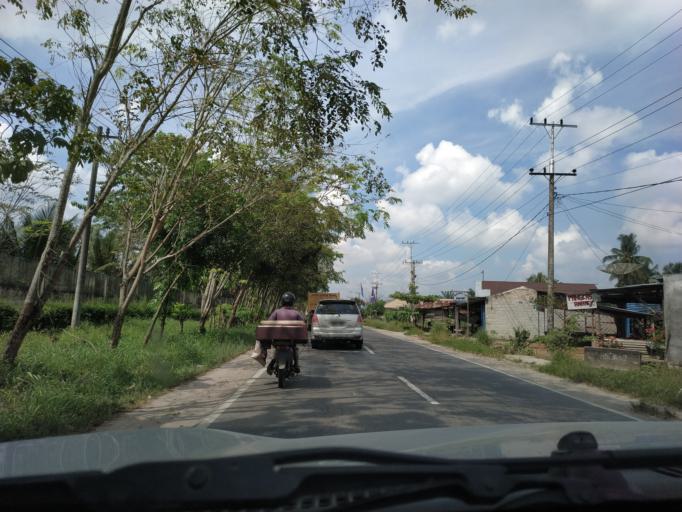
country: ID
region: North Sumatra
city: Tanjungbalai
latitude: 2.9247
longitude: 99.7360
